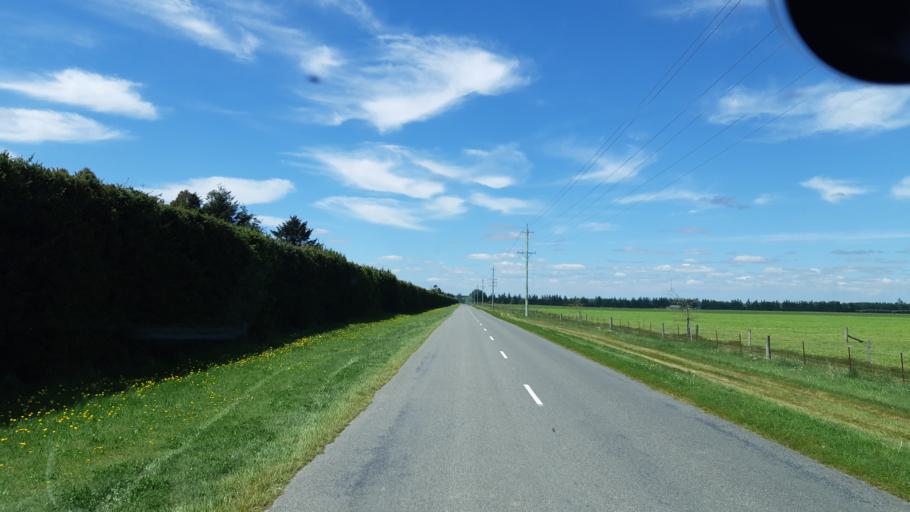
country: NZ
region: Canterbury
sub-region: Ashburton District
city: Methven
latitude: -43.7259
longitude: 171.4940
